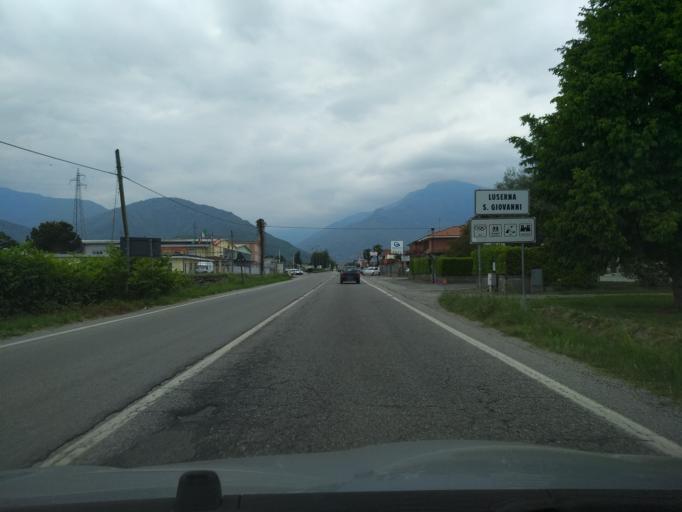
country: IT
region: Piedmont
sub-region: Provincia di Torino
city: Bibiana
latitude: 44.8109
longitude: 7.2756
